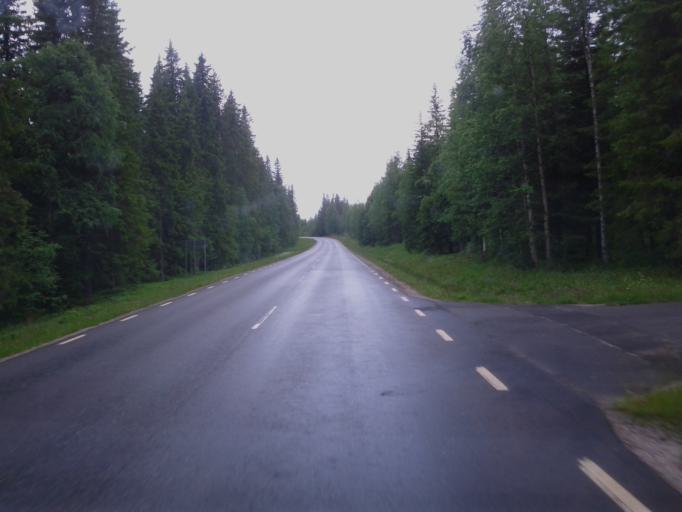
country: SE
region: Vaesterbotten
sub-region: Mala Kommun
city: Mala
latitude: 65.0969
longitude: 18.9218
